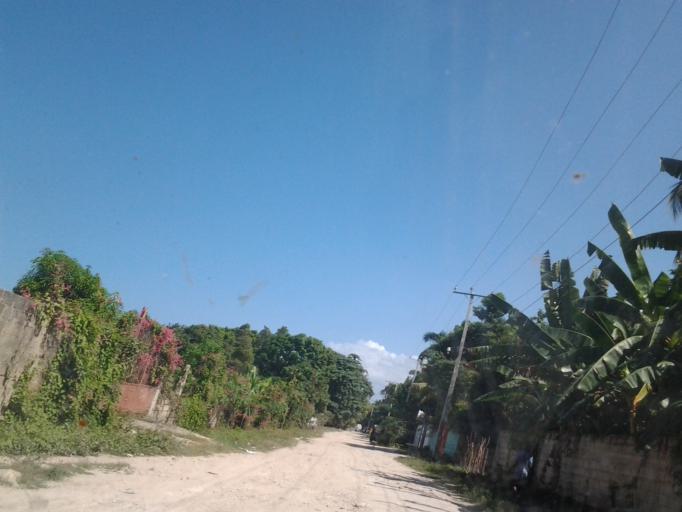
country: HT
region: Ouest
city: Grangwav
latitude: 18.4259
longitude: -72.7760
